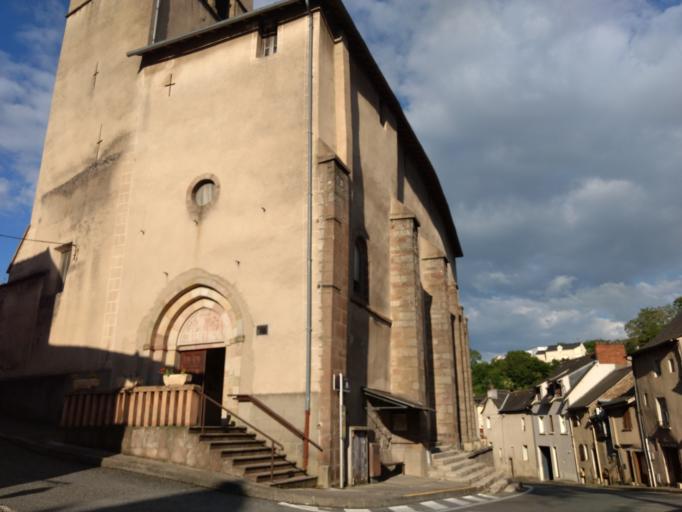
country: FR
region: Midi-Pyrenees
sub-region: Departement de l'Aveyron
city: Le Monastere
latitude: 44.3426
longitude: 2.5779
